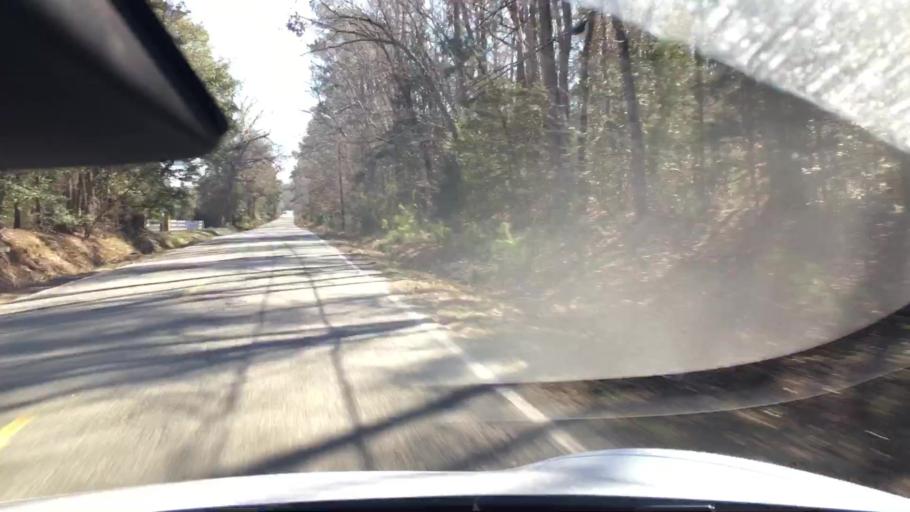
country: US
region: Virginia
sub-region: Henrico County
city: Short Pump
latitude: 37.5833
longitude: -77.7451
